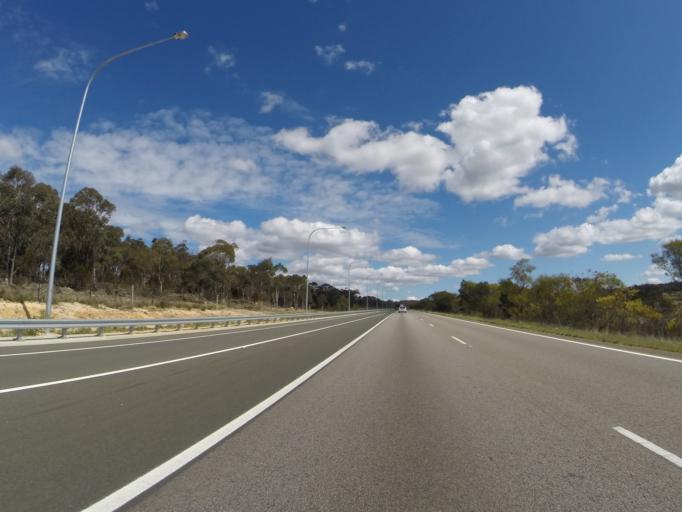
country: AU
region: New South Wales
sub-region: Goulburn Mulwaree
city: Goulburn
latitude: -34.7323
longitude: 149.9765
